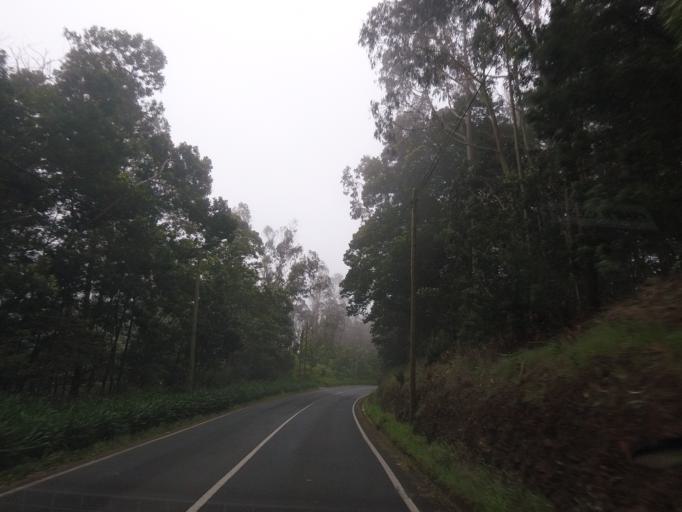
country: PT
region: Madeira
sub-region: Santa Cruz
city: Santa Cruz
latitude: 32.7149
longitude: -16.7973
